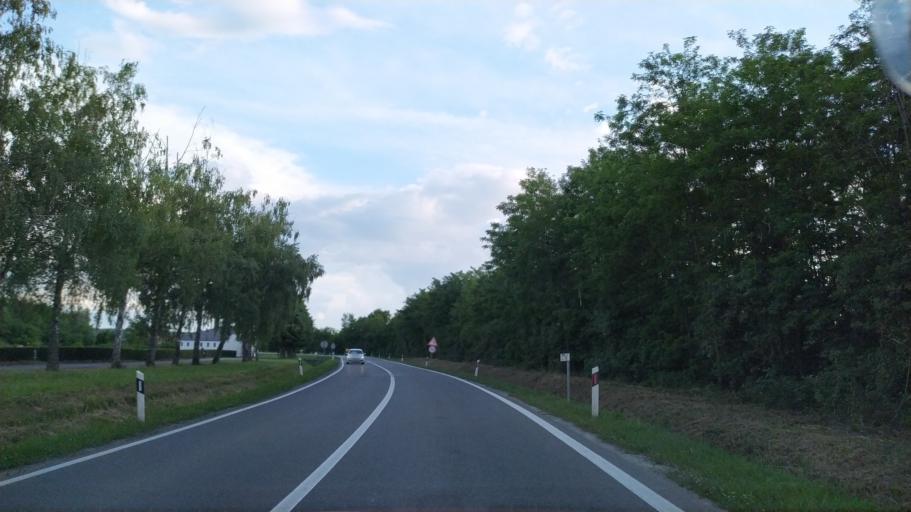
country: HR
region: Osjecko-Baranjska
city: Fericanci
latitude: 45.5032
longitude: 18.0123
